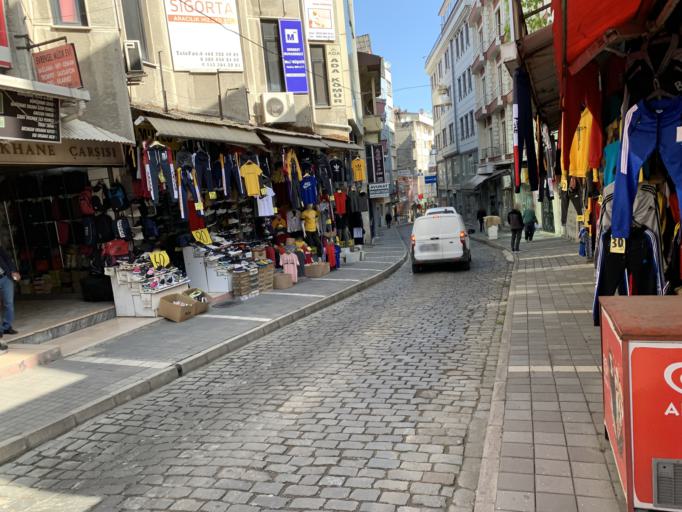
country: TR
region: Trabzon
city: Trabzon
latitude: 41.0052
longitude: 39.7226
